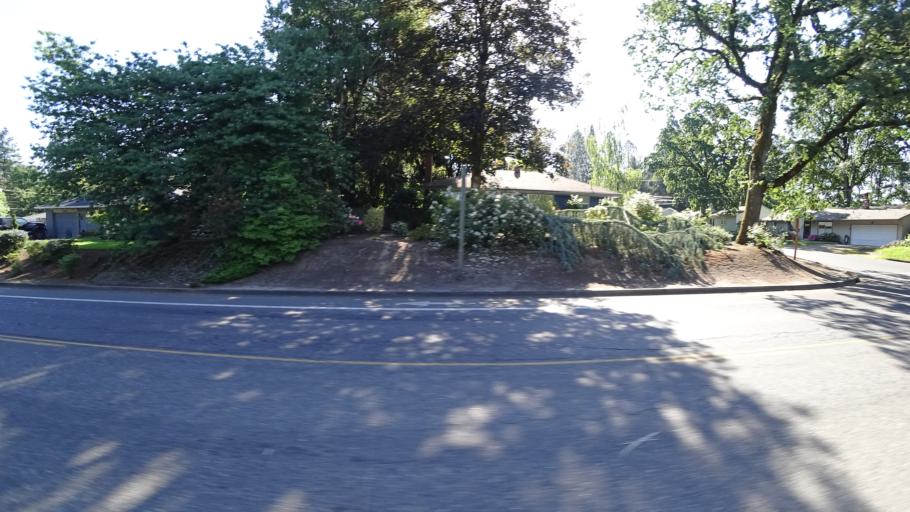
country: US
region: Oregon
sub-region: Washington County
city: Metzger
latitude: 45.4435
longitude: -122.7657
